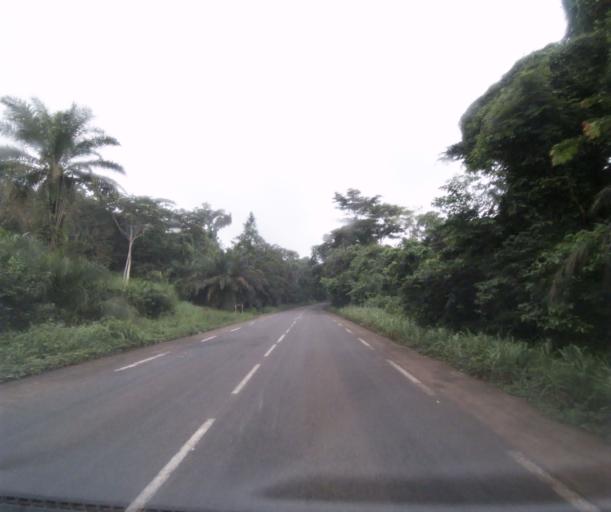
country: CM
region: Centre
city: Eseka
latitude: 3.8809
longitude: 10.6938
